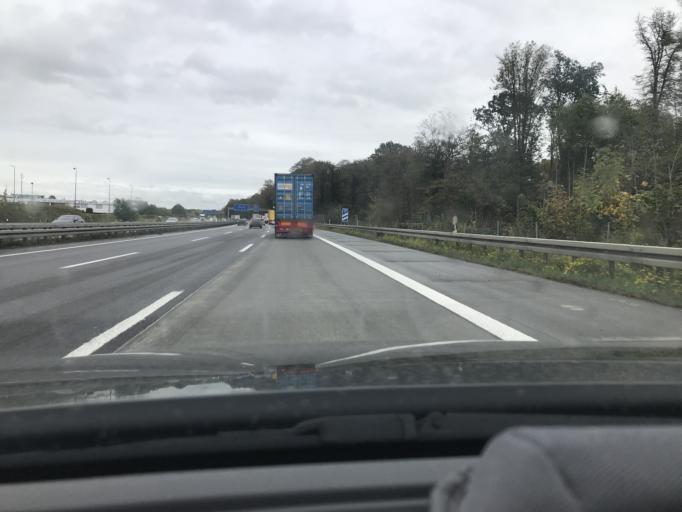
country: DE
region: North Rhine-Westphalia
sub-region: Regierungsbezirk Koln
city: Kerpen
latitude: 50.8896
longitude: 6.6713
